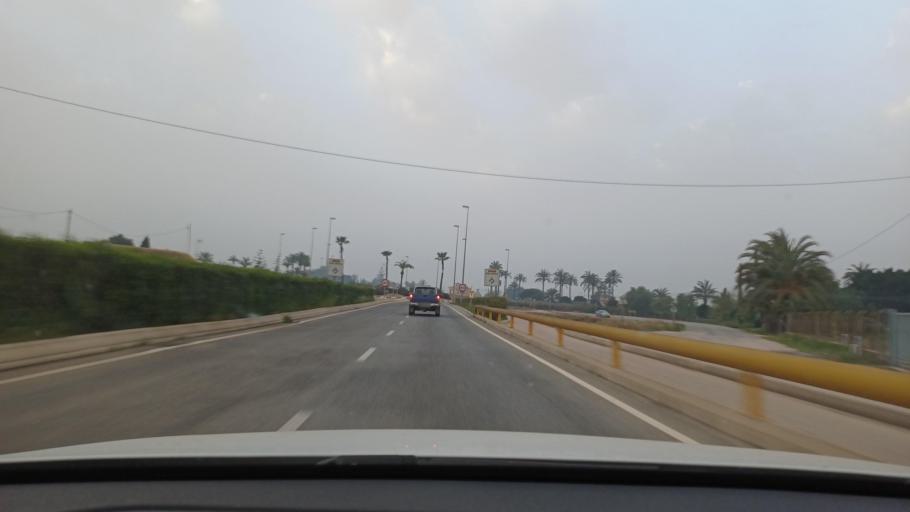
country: ES
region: Valencia
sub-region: Provincia de Alicante
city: Elche
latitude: 38.2066
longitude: -0.6988
